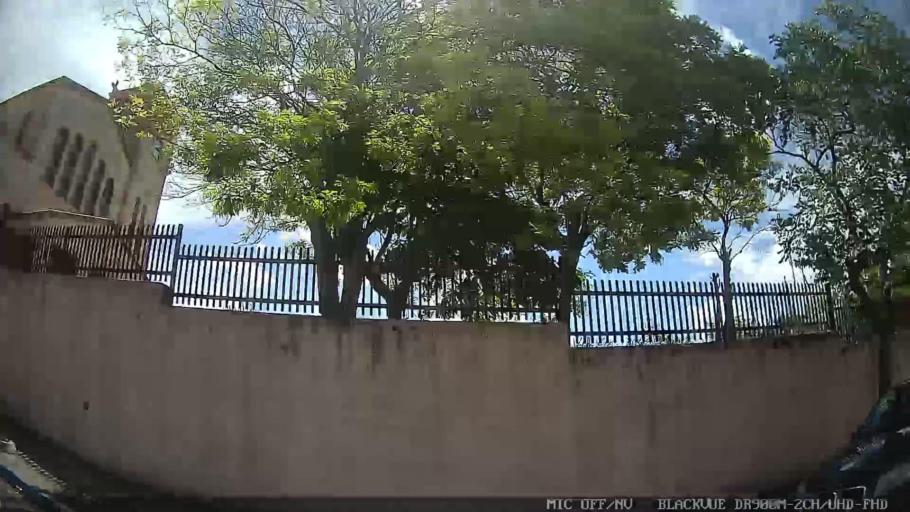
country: BR
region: Sao Paulo
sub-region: Conchas
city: Conchas
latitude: -23.0154
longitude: -48.0101
